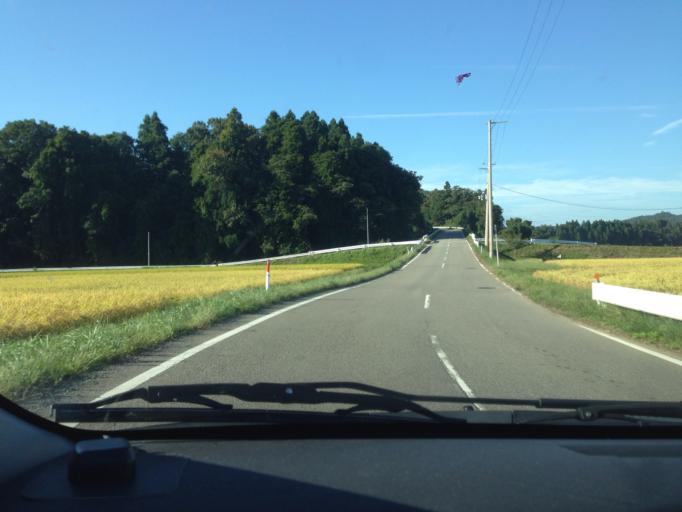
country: JP
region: Fukushima
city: Kitakata
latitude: 37.5904
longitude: 139.8132
